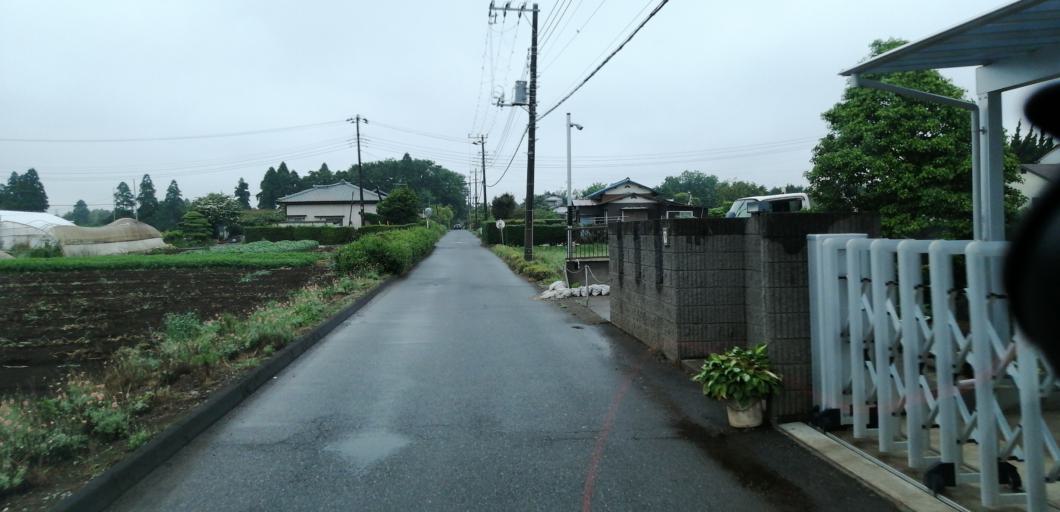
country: JP
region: Chiba
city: Yachimata
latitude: 35.5935
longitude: 140.2766
